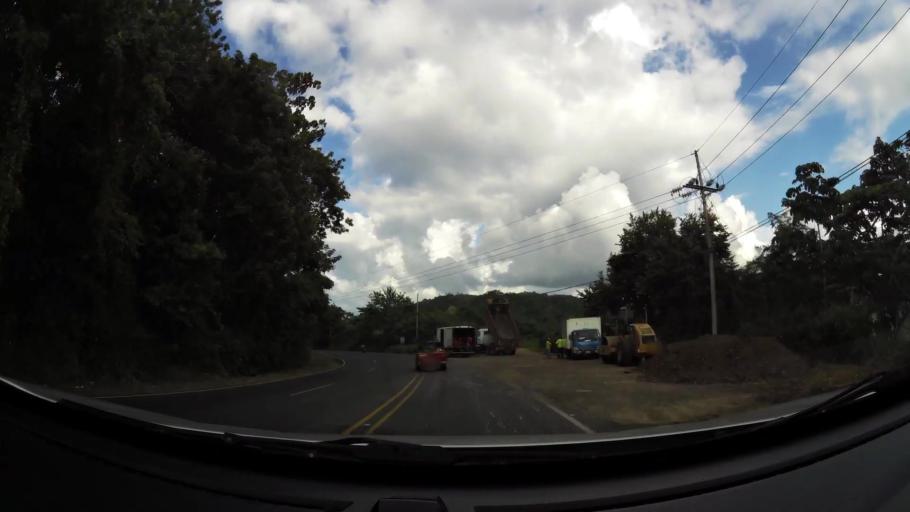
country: CR
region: Puntarenas
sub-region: Canton de Garabito
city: Jaco
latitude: 9.6895
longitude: -84.6447
